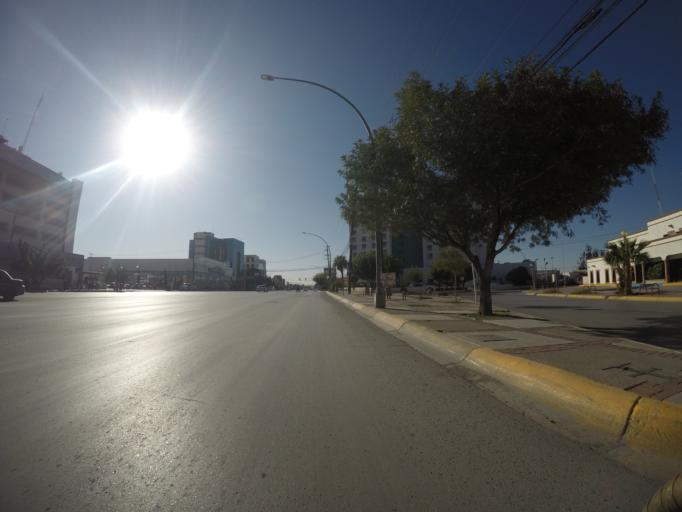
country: MX
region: Chihuahua
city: Ciudad Juarez
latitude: 31.7374
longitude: -106.4522
